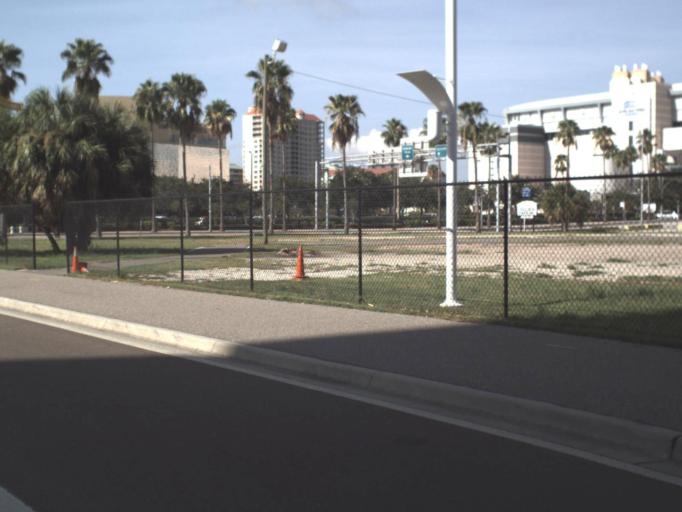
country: US
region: Florida
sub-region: Hillsborough County
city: Tampa
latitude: 27.9442
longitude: -82.4489
